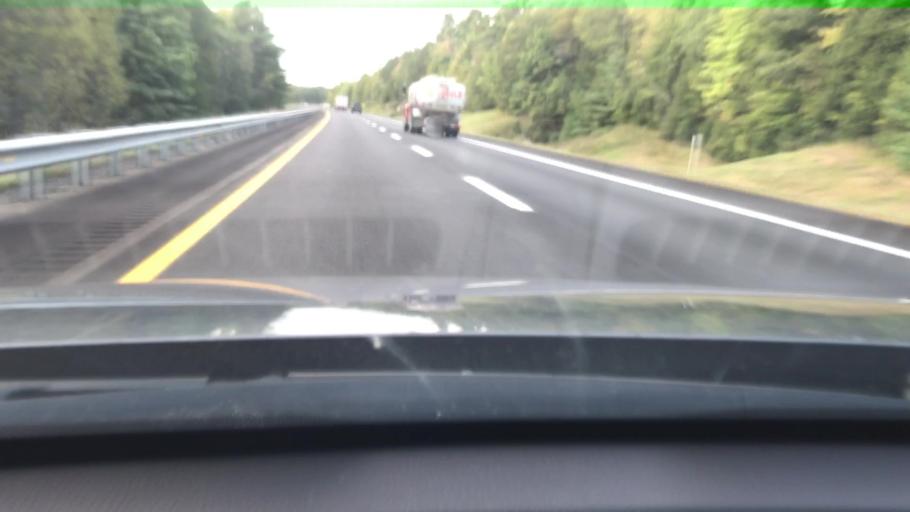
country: US
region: Maine
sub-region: Sagadahoc County
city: Richmond
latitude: 44.0520
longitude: -69.8927
